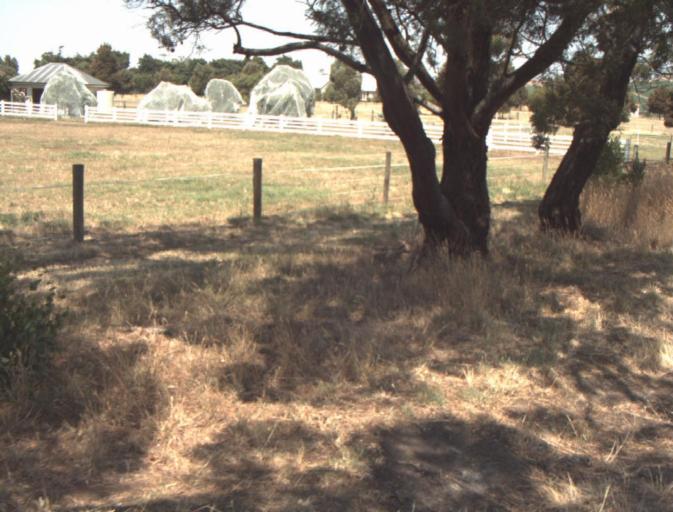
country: AU
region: Tasmania
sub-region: Launceston
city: Newstead
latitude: -41.5007
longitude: 147.2061
